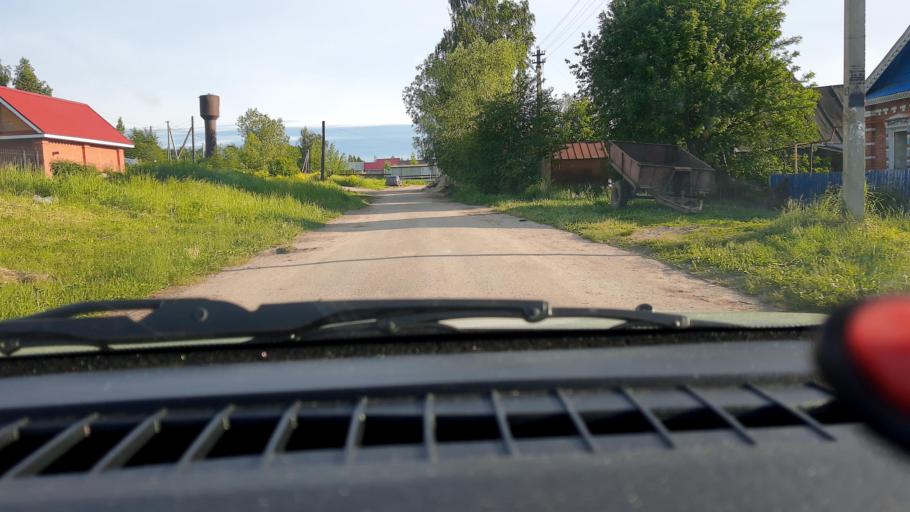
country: RU
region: Nizjnij Novgorod
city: Afonino
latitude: 56.1237
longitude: 44.0254
